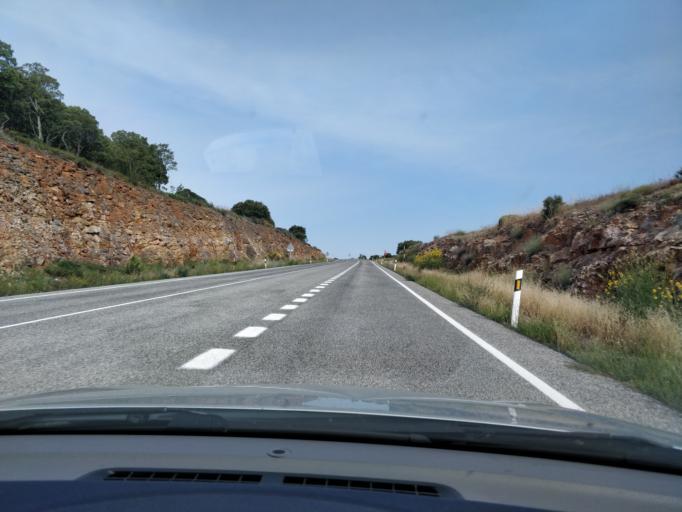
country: ES
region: Castille and Leon
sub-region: Provincia de Burgos
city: Medina de Pomar
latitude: 42.9237
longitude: -3.6288
